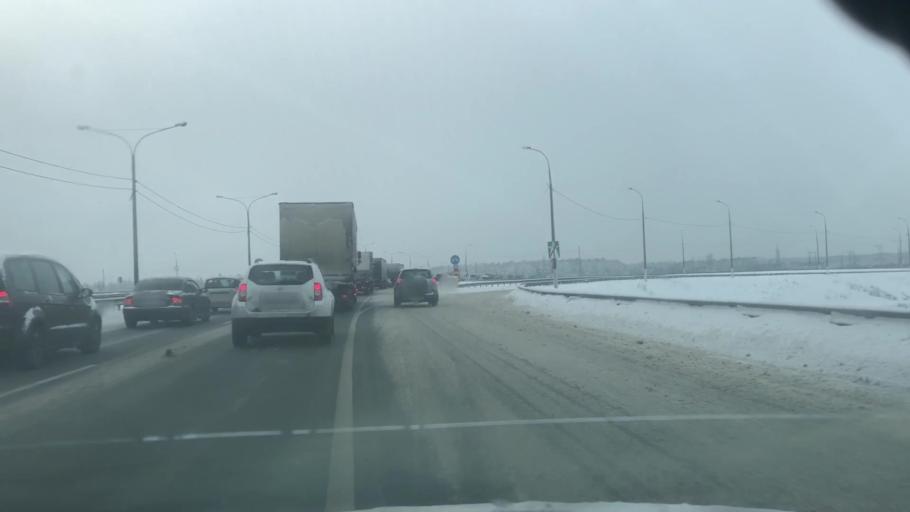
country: RU
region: Moskovskaya
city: Mikhnevo
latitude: 55.0796
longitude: 37.9364
